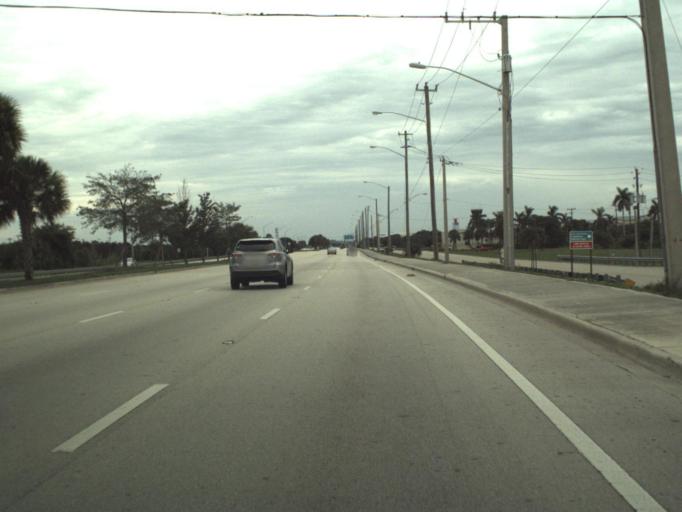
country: US
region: Florida
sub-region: Palm Beach County
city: Haverhill
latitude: 26.6774
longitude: -80.0914
